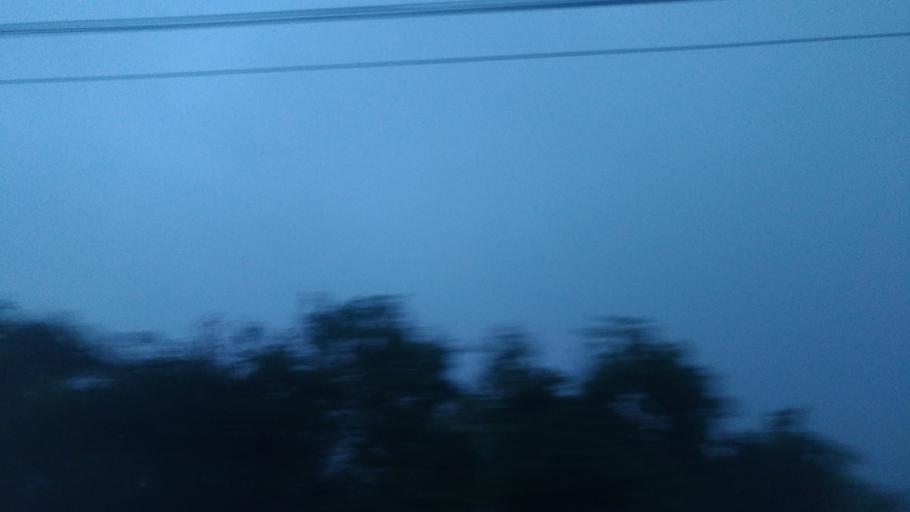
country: TW
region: Taiwan
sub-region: Miaoli
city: Miaoli
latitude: 24.5401
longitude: 120.6962
